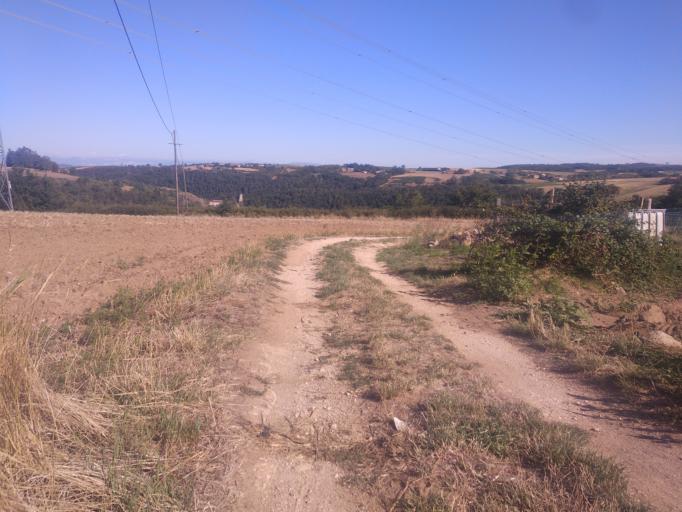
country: FR
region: Rhone-Alpes
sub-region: Departement de l'Ardeche
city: Vernosc-les-Annonay
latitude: 45.1937
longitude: 4.7509
